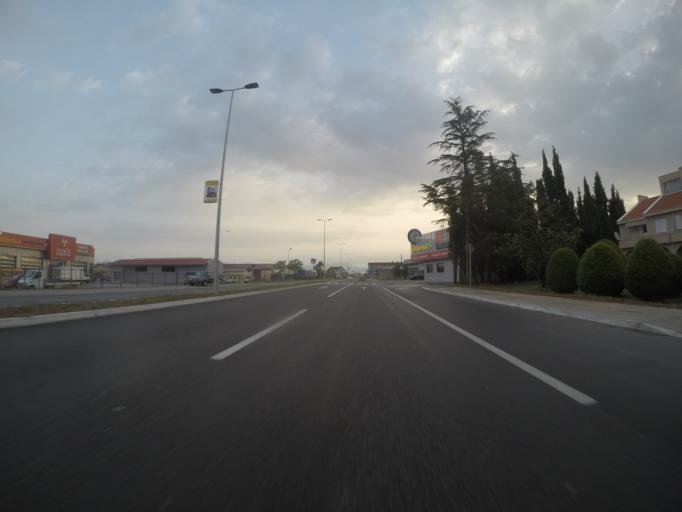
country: ME
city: Mojanovici
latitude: 42.3602
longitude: 19.2246
